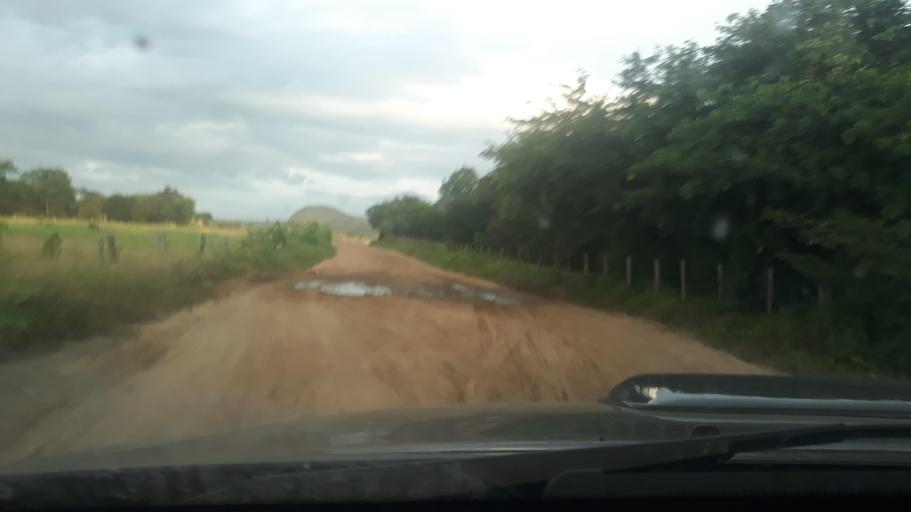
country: BR
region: Bahia
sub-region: Riacho De Santana
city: Riacho de Santana
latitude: -13.9003
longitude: -42.8705
